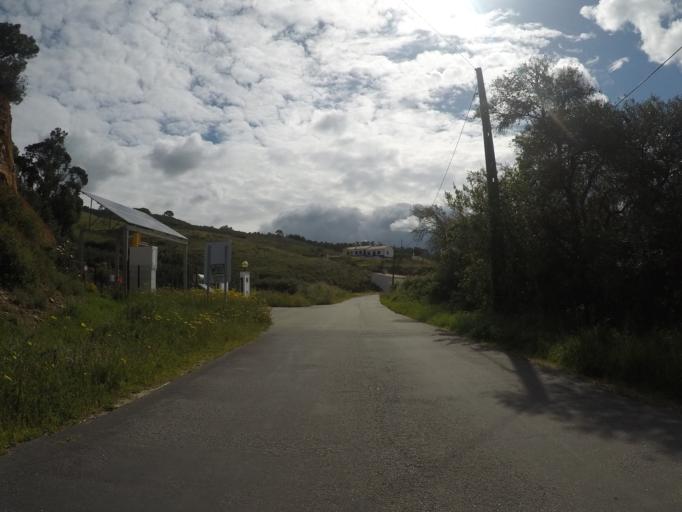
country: PT
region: Beja
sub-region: Odemira
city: Sao Teotonio
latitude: 37.4367
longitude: -8.7688
